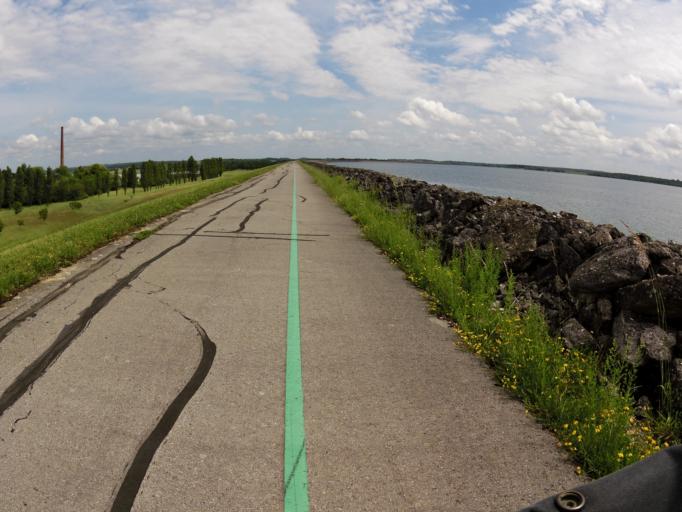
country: FR
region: Champagne-Ardenne
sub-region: Departement de l'Aube
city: Piney
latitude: 48.3416
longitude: 4.4011
